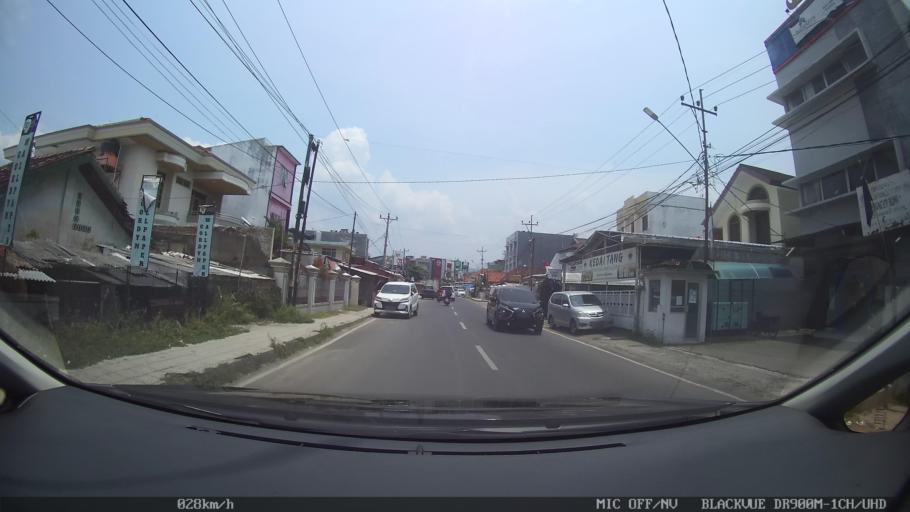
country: ID
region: Lampung
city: Bandarlampung
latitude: -5.4395
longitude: 105.2669
